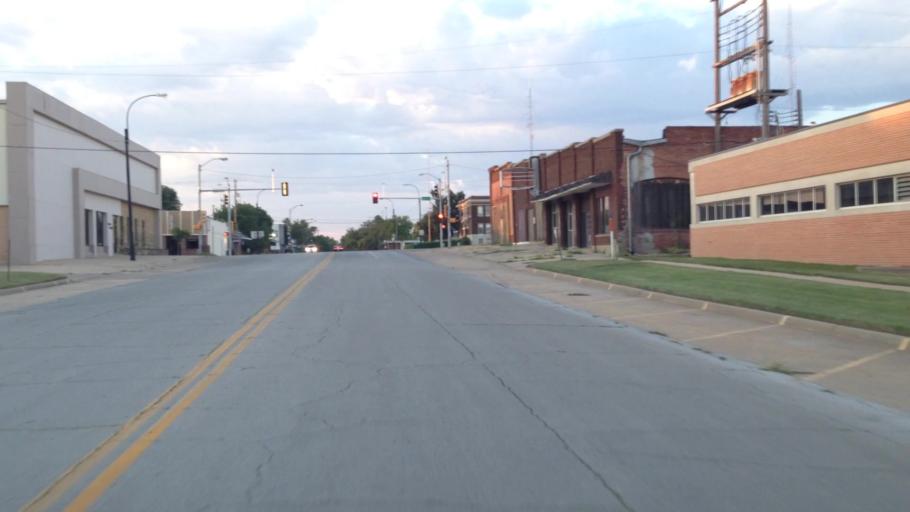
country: US
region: Kansas
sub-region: Montgomery County
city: Independence
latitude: 37.2223
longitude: -95.7053
